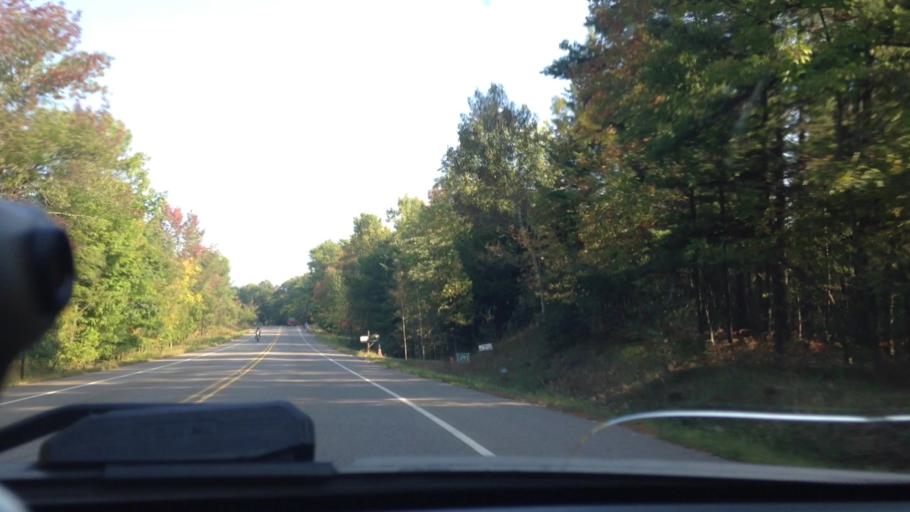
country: US
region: Michigan
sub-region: Dickinson County
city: Quinnesec
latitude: 45.8123
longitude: -87.9855
